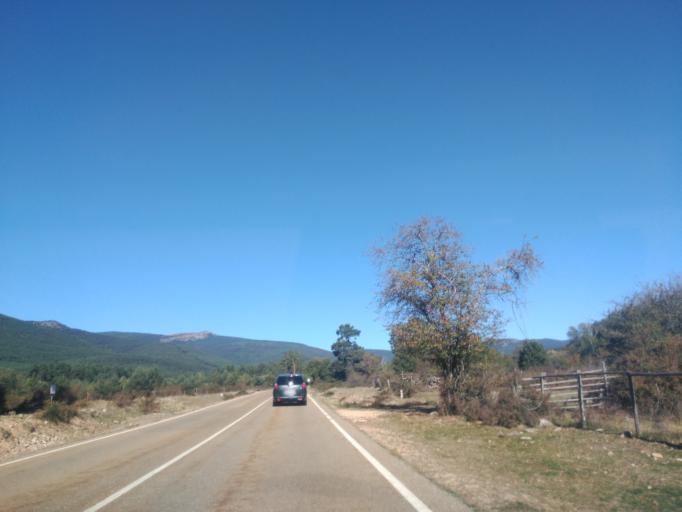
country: ES
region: Castille and Leon
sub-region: Provincia de Soria
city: Vinuesa
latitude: 41.9614
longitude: -2.7781
